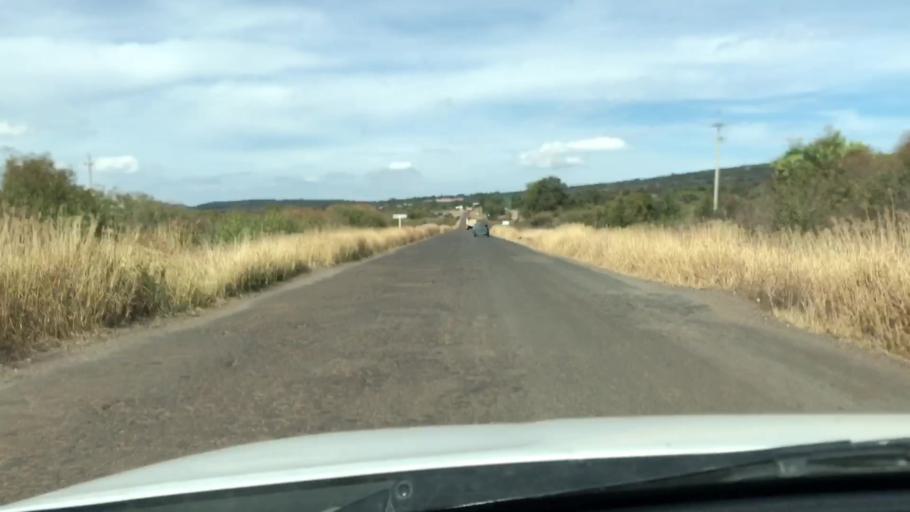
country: MX
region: Jalisco
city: Chiquilistlan
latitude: 20.1624
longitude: -103.7247
